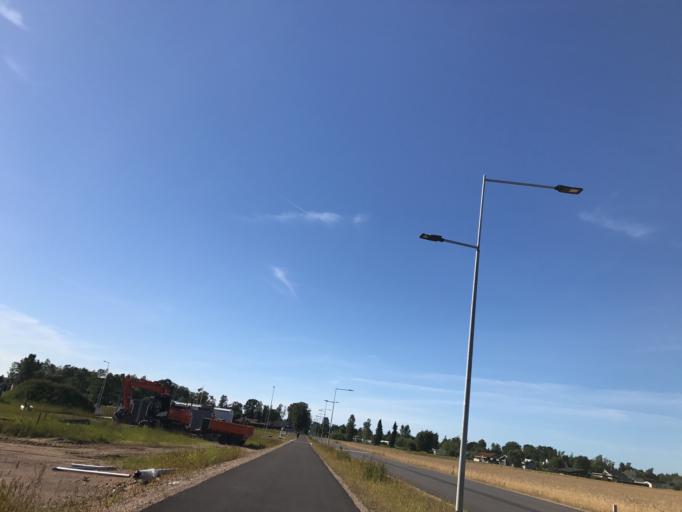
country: SE
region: Skane
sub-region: Bastads Kommun
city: Bastad
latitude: 56.4340
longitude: 12.9068
